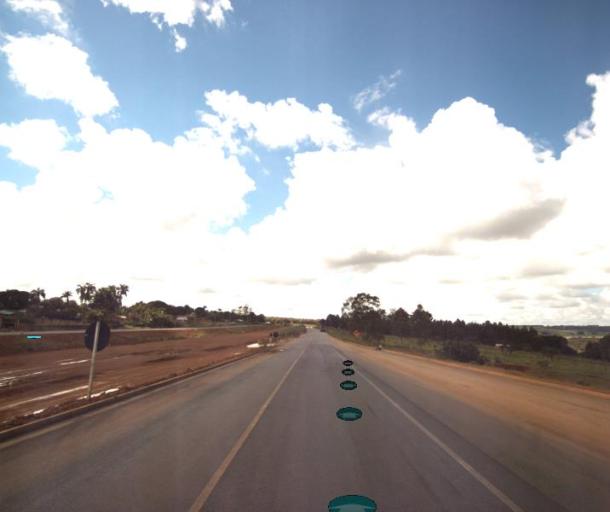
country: BR
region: Goias
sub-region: Anapolis
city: Anapolis
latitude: -16.1920
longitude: -49.0326
